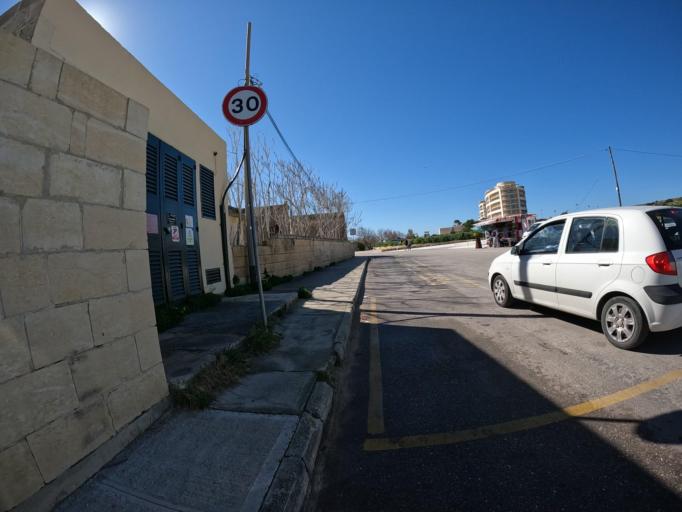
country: MT
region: L-Imgarr
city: Imgarr
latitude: 35.9353
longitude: 14.3469
